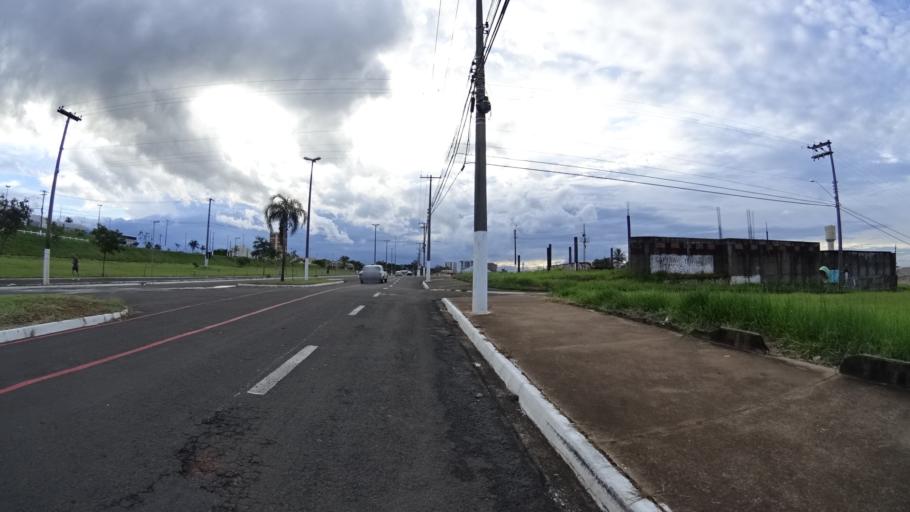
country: BR
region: Sao Paulo
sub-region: Marilia
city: Marilia
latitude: -22.2287
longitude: -49.9214
